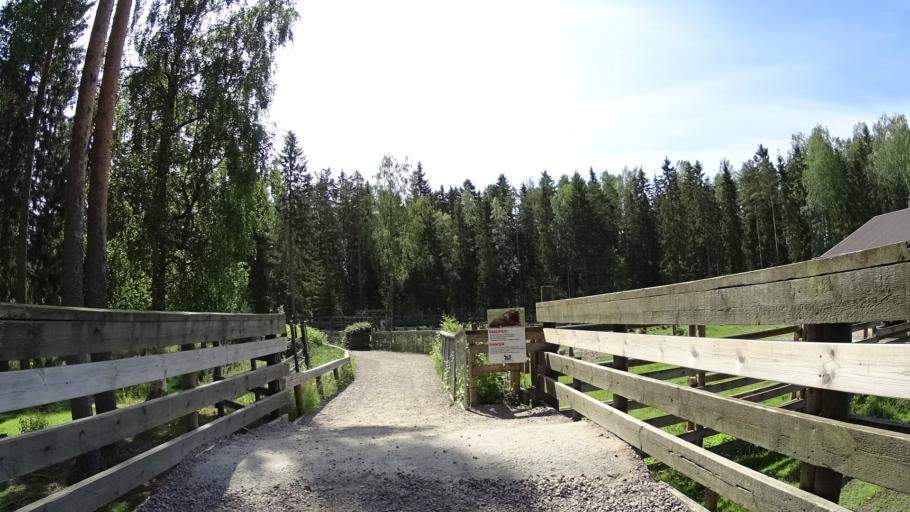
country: FI
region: Southern Ostrobothnia
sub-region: Kuusiokunnat
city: AEhtaeri
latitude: 62.5403
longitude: 24.1811
